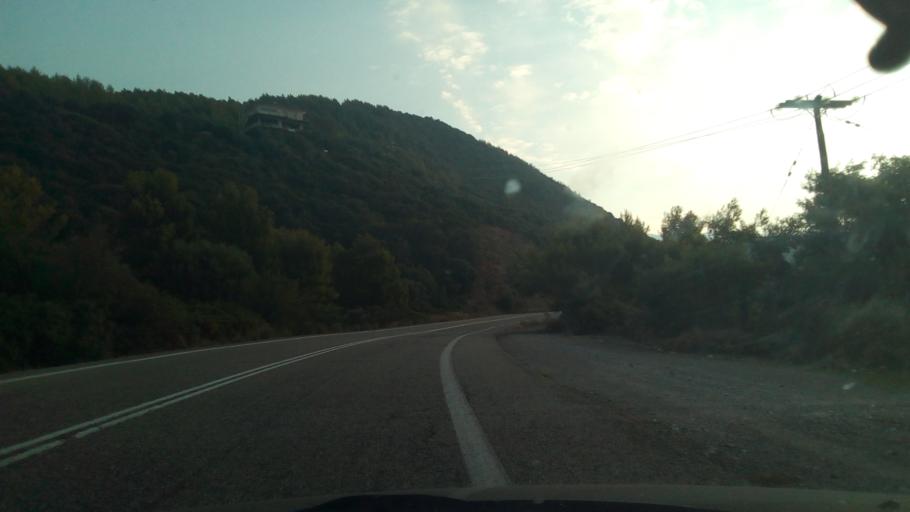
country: GR
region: West Greece
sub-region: Nomos Aitolias kai Akarnanias
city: Nafpaktos
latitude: 38.4071
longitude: 21.9312
